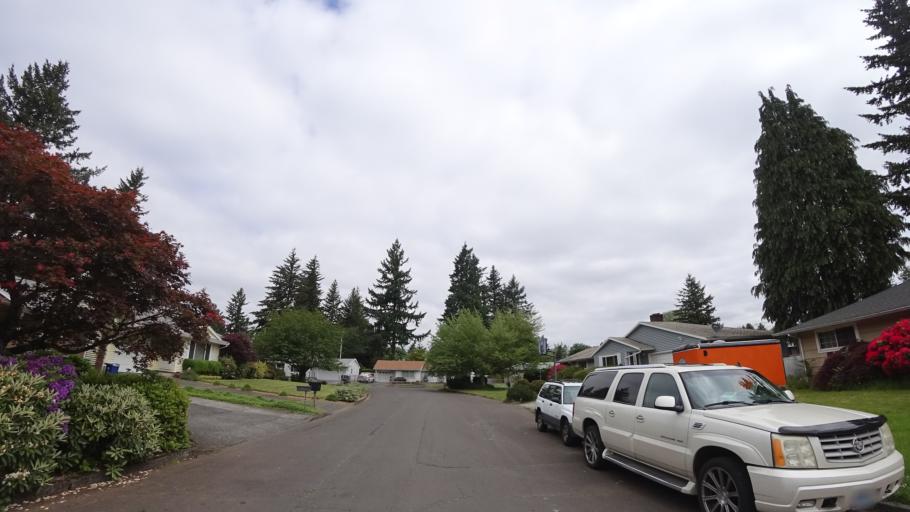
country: US
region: Oregon
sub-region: Multnomah County
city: Gresham
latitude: 45.5001
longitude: -122.4828
